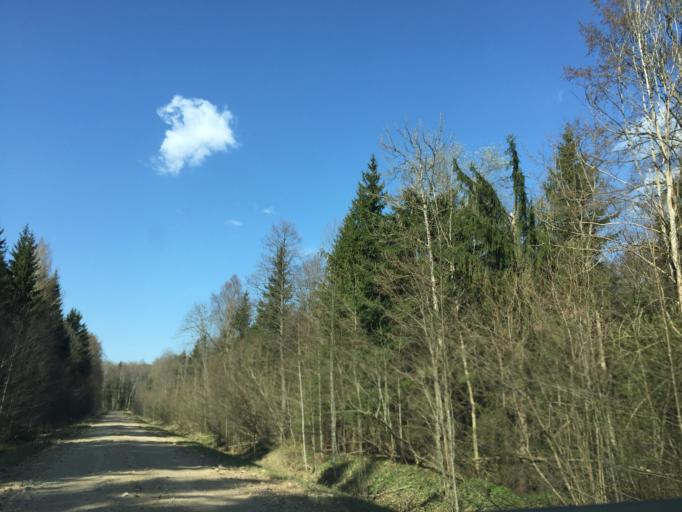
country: LV
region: Lielvarde
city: Lielvarde
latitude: 56.8517
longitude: 24.8037
